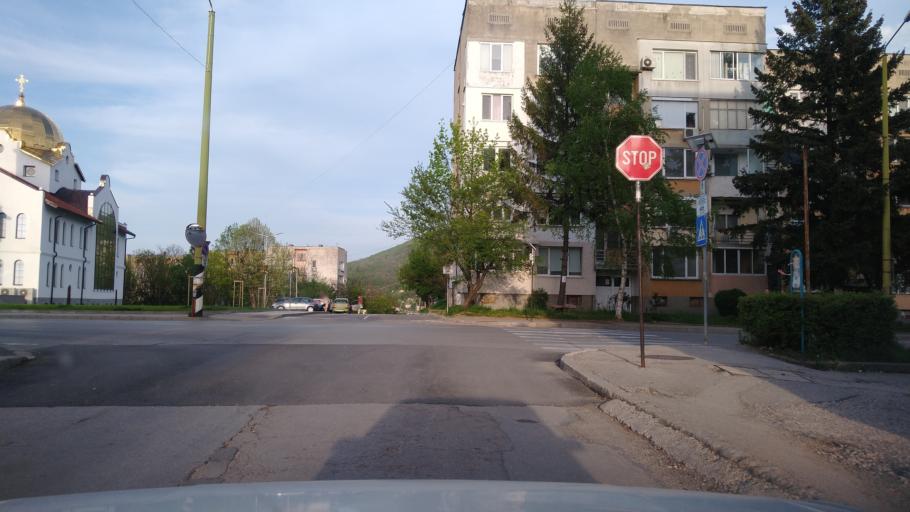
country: BG
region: Gabrovo
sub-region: Obshtina Gabrovo
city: Gabrovo
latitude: 42.8884
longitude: 25.3132
